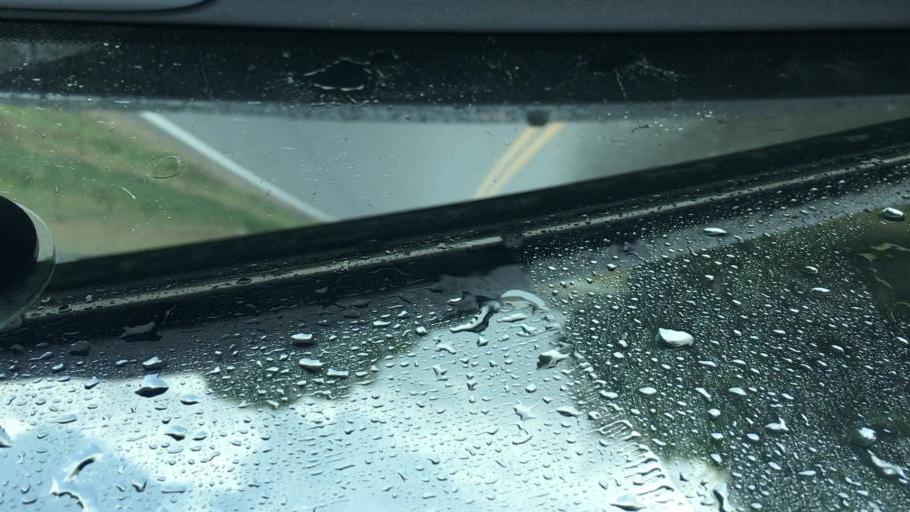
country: US
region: Oklahoma
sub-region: Johnston County
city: Tishomingo
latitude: 34.1802
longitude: -96.7151
